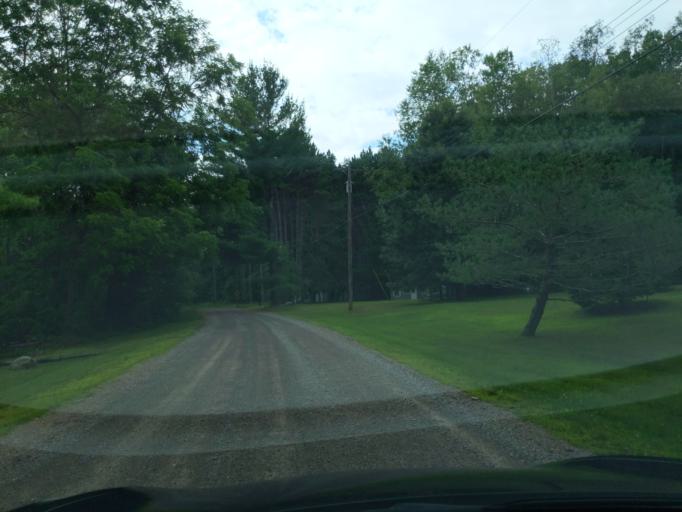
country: US
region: Michigan
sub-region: Clare County
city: Harrison
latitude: 43.9780
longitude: -85.0014
